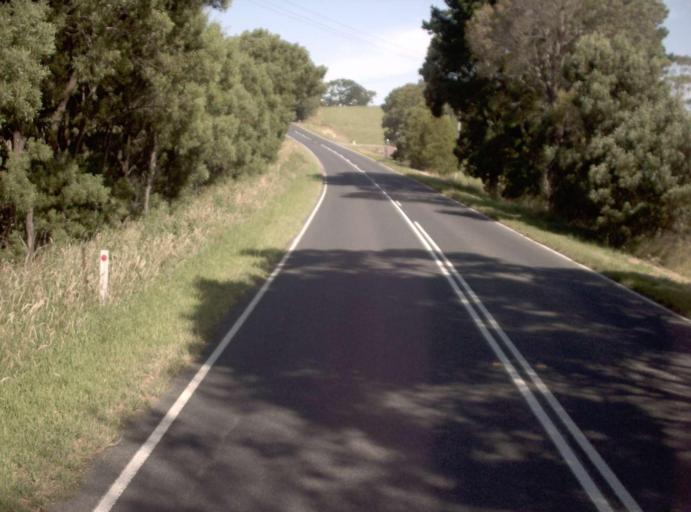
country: AU
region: Victoria
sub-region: Baw Baw
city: Warragul
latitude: -38.3583
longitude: 145.8052
